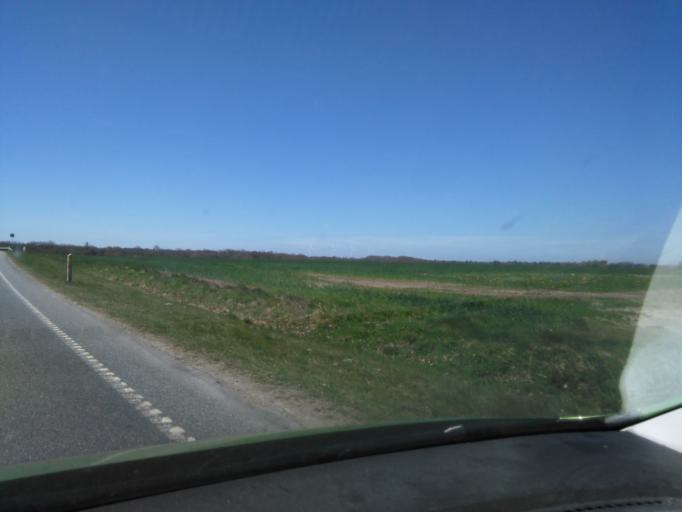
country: DK
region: South Denmark
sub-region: Varde Kommune
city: Olgod
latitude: 55.6857
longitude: 8.5949
